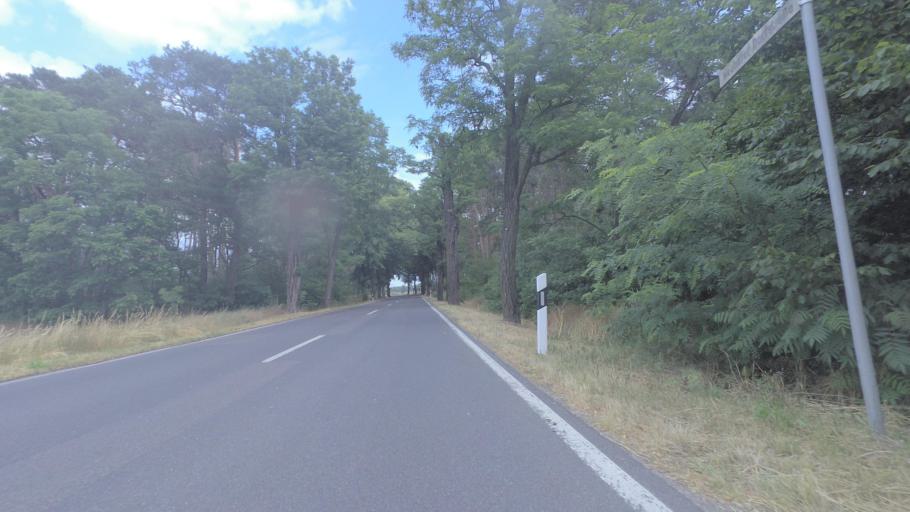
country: DE
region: Brandenburg
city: Am Mellensee
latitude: 52.1331
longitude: 13.4635
